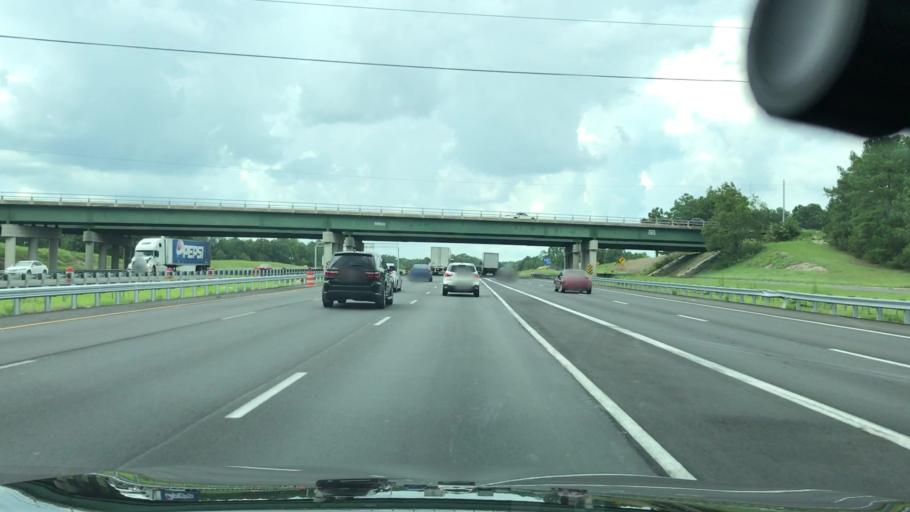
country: US
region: South Carolina
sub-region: Richland County
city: Dentsville
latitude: 34.0993
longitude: -80.9578
